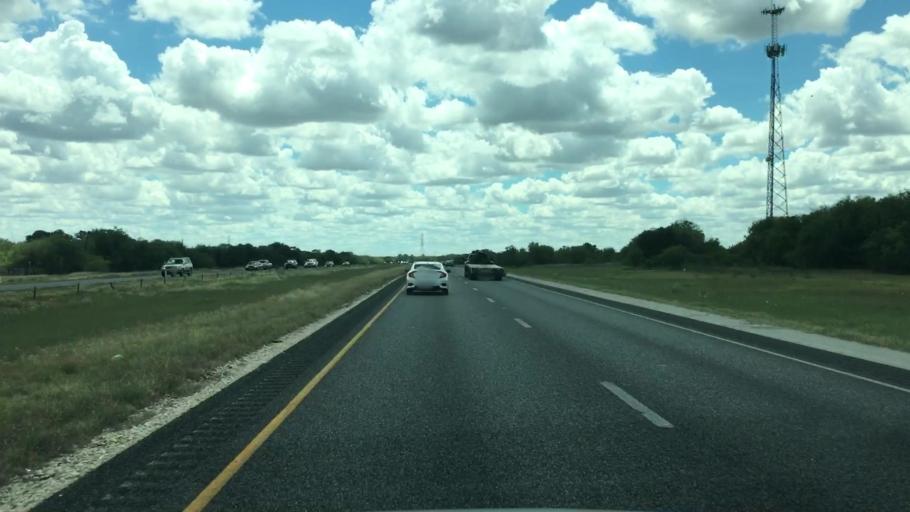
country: US
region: Texas
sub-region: Bexar County
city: Elmendorf
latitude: 29.2602
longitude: -98.3955
